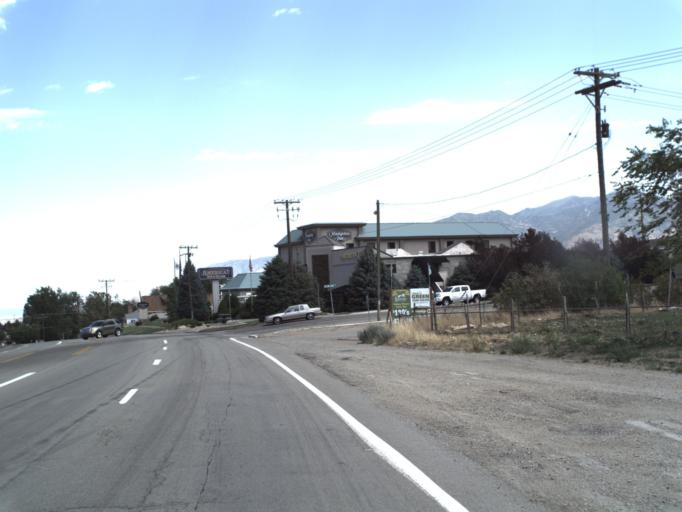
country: US
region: Utah
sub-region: Tooele County
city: Tooele
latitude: 40.5180
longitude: -112.3013
